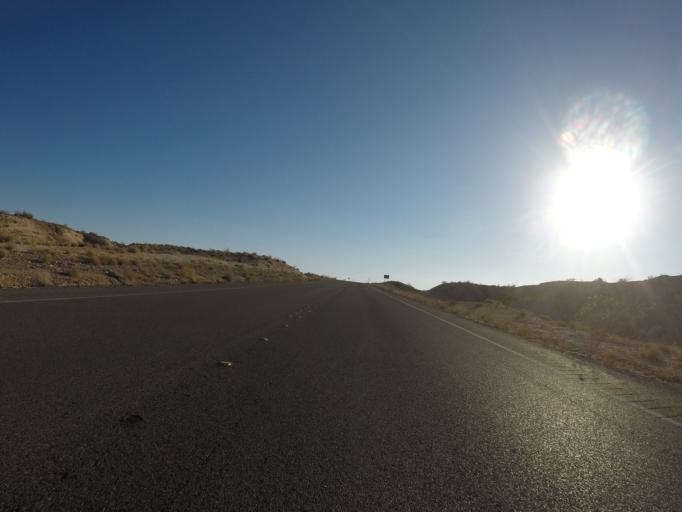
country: US
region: Nevada
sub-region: Clark County
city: Moapa Valley
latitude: 36.3962
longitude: -114.4244
